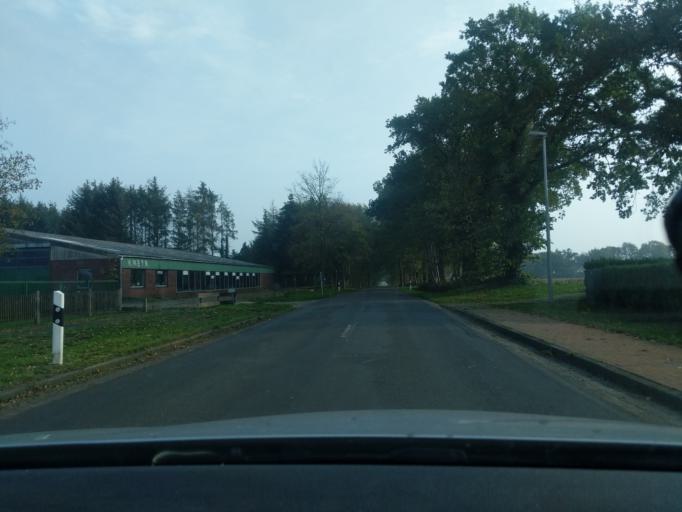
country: DE
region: Lower Saxony
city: Stinstedt
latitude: 53.6591
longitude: 8.9749
